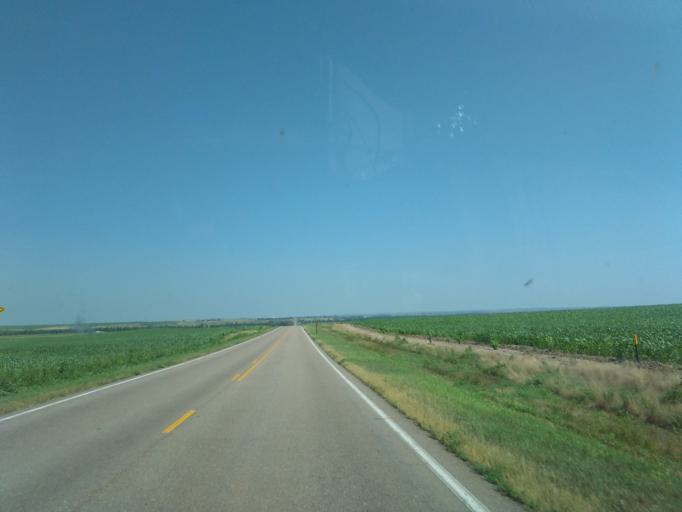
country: US
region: Nebraska
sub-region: Dundy County
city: Benkelman
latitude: 39.9817
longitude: -101.5419
